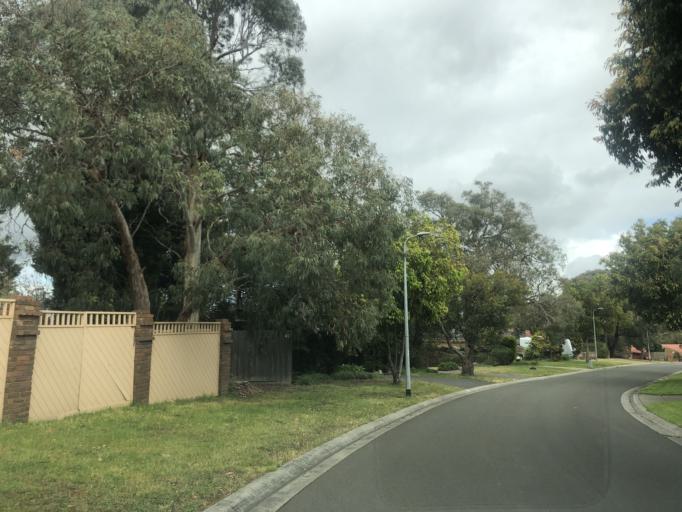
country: AU
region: Victoria
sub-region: Knox
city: Rowville
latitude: -37.9368
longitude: 145.2291
